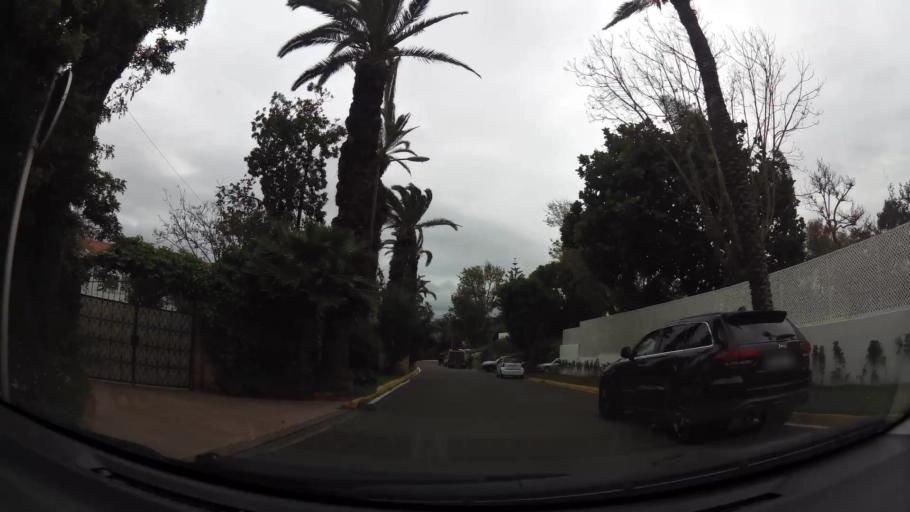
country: MA
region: Grand Casablanca
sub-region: Casablanca
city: Casablanca
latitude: 33.5853
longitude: -7.6617
